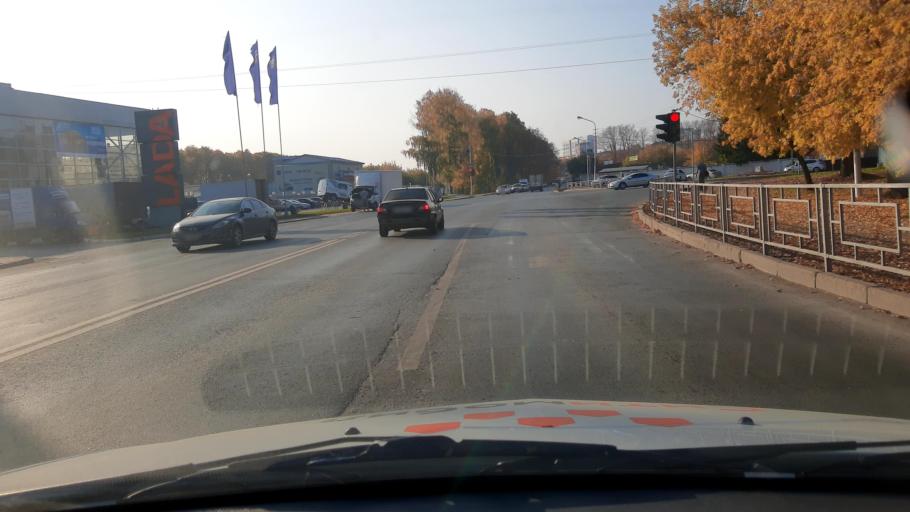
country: RU
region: Bashkortostan
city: Ufa
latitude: 54.8104
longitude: 56.0819
